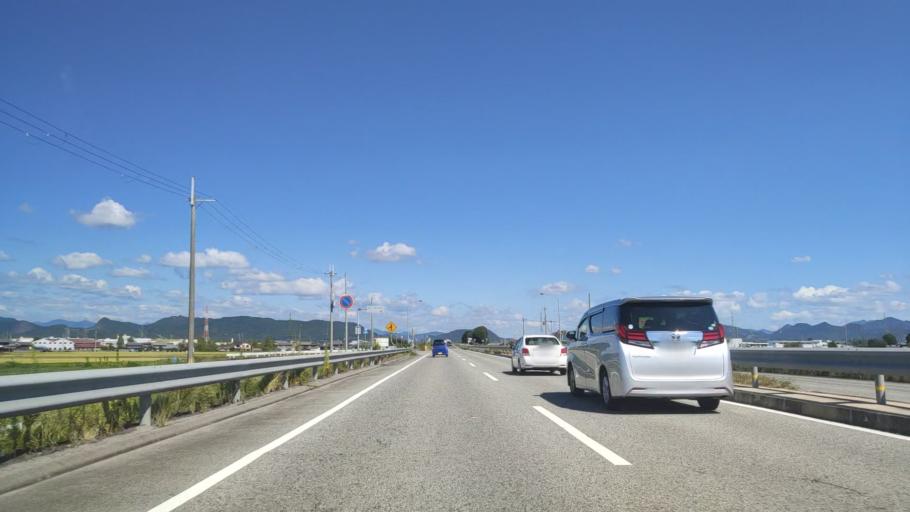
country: JP
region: Hyogo
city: Yashiro
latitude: 34.9008
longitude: 134.9519
